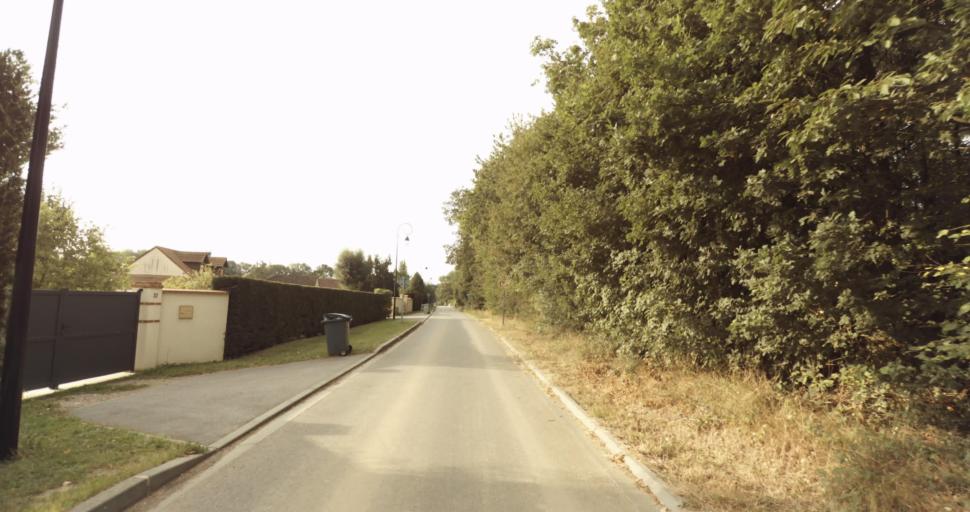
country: FR
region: Centre
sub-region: Departement d'Eure-et-Loir
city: Vert-en-Drouais
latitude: 48.7858
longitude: 1.3154
